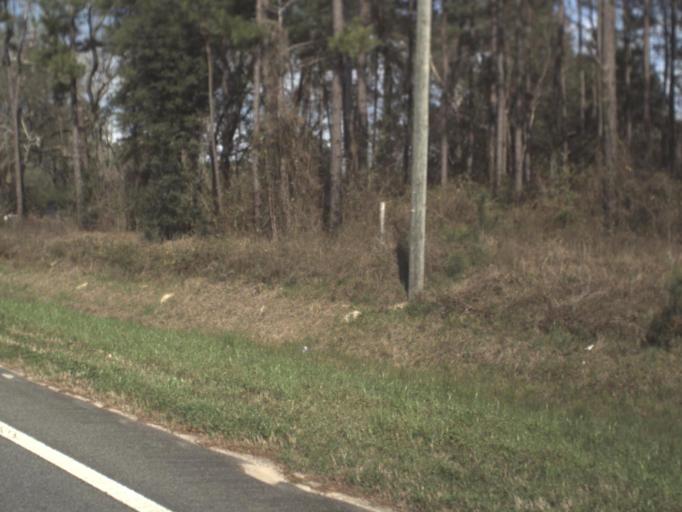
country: US
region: Florida
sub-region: Gadsden County
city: Quincy
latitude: 30.5910
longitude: -84.5054
